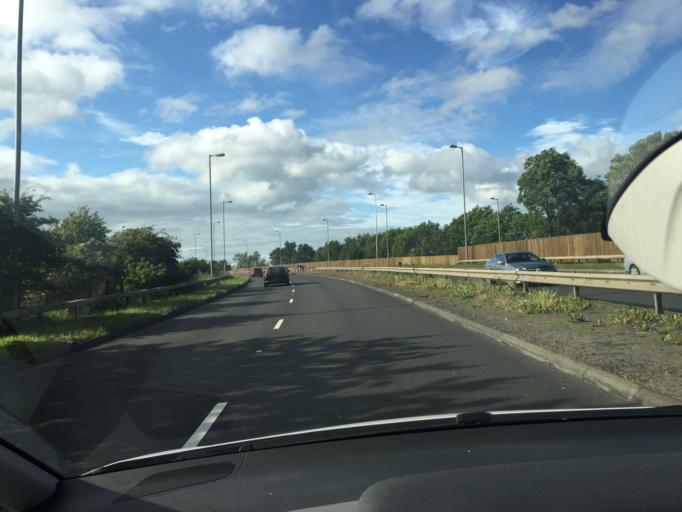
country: GB
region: Scotland
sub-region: North Lanarkshire
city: Bellshill
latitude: 55.8119
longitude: -4.0380
